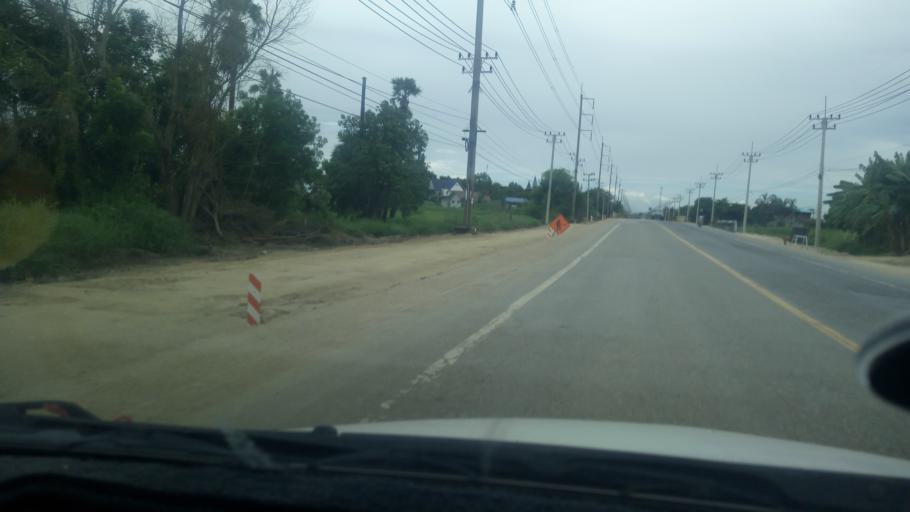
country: TH
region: Chon Buri
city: Phan Thong
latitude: 13.5235
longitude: 101.1533
